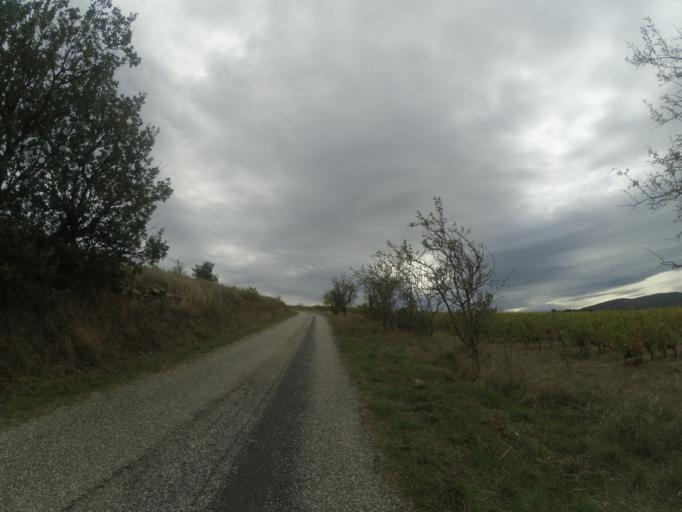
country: FR
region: Languedoc-Roussillon
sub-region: Departement des Pyrenees-Orientales
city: Estagel
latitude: 42.7358
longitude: 2.6789
